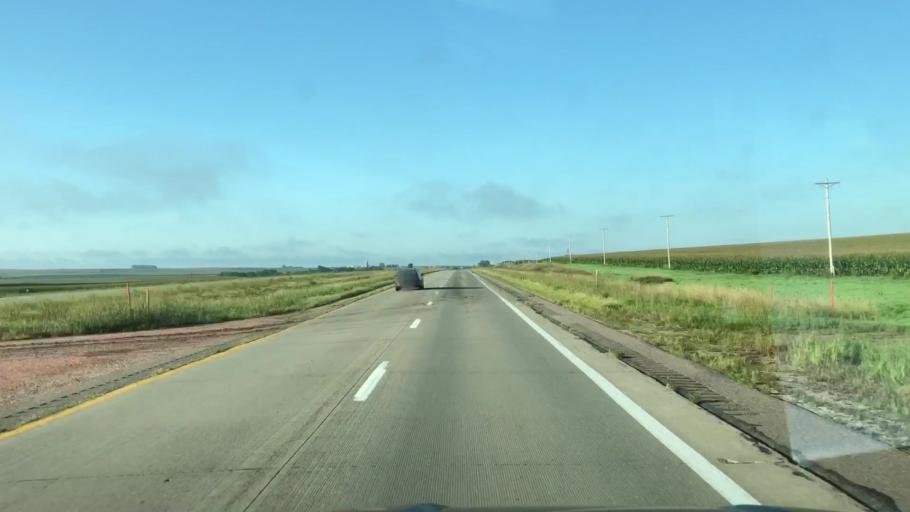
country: US
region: Iowa
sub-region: Sioux County
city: Alton
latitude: 42.9435
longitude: -96.0413
